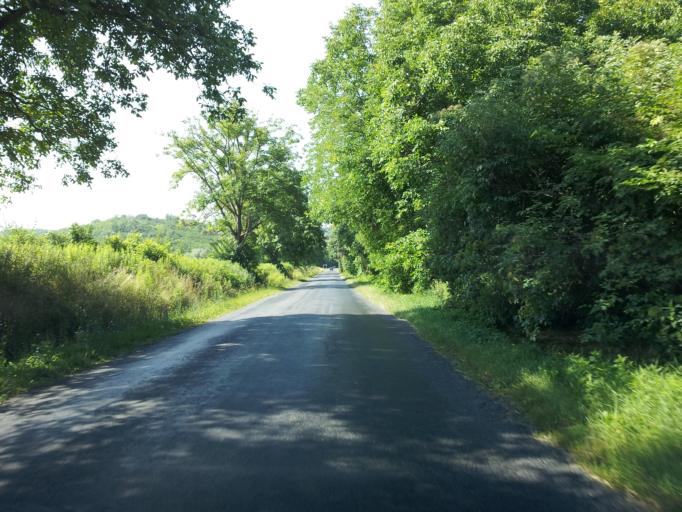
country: HU
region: Zala
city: Heviz
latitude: 46.8608
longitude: 17.1358
